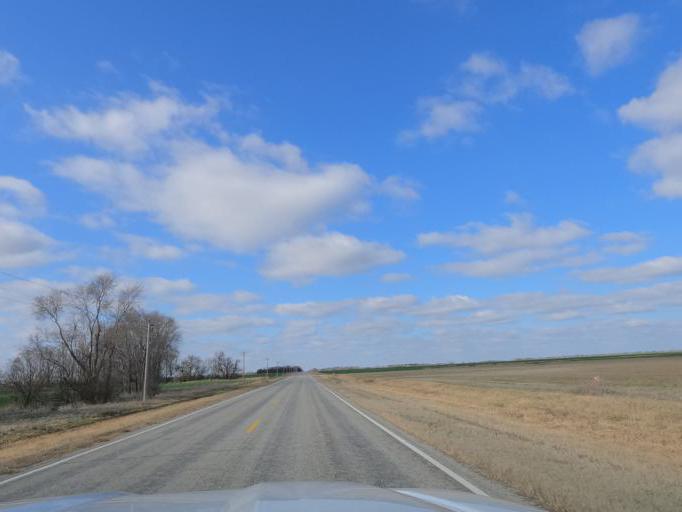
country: US
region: Kansas
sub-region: McPherson County
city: Inman
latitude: 38.1941
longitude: -97.8486
